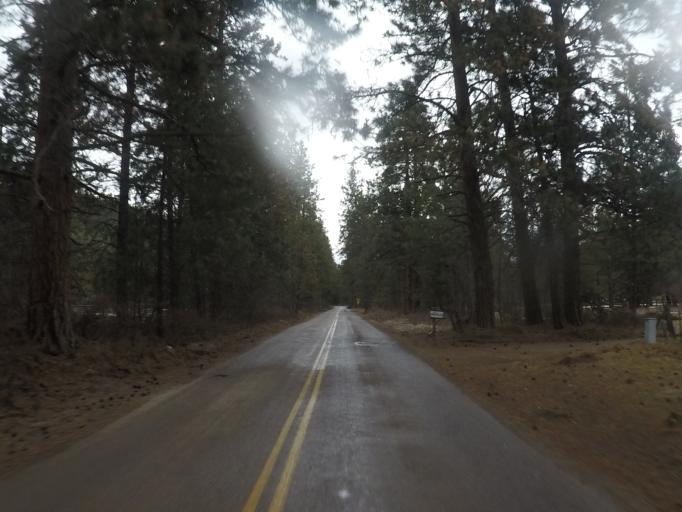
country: US
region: Montana
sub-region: Missoula County
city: East Missoula
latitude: 46.9152
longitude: -113.9603
